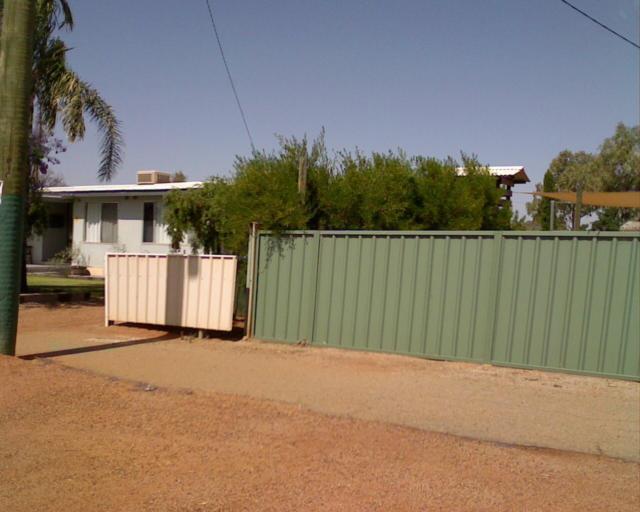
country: AU
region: Western Australia
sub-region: Merredin
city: Merredin
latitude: -30.9170
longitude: 118.2061
